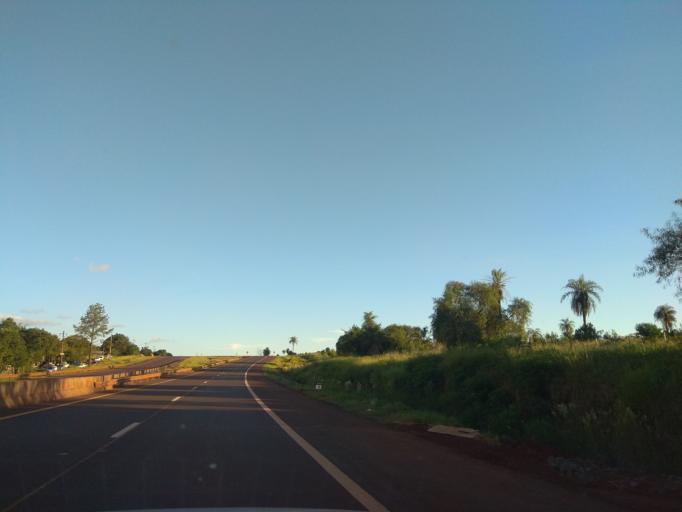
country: AR
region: Misiones
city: Garupa
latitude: -27.5308
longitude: -55.8570
